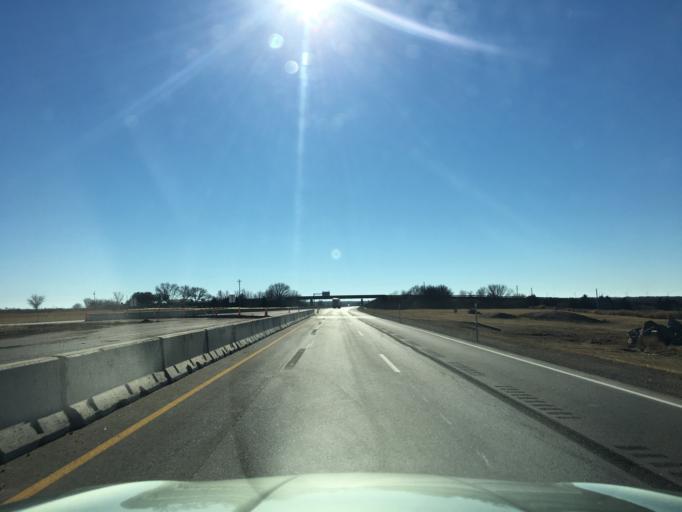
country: US
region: Kansas
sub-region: Sumner County
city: Wellington
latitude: 37.2354
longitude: -97.3391
